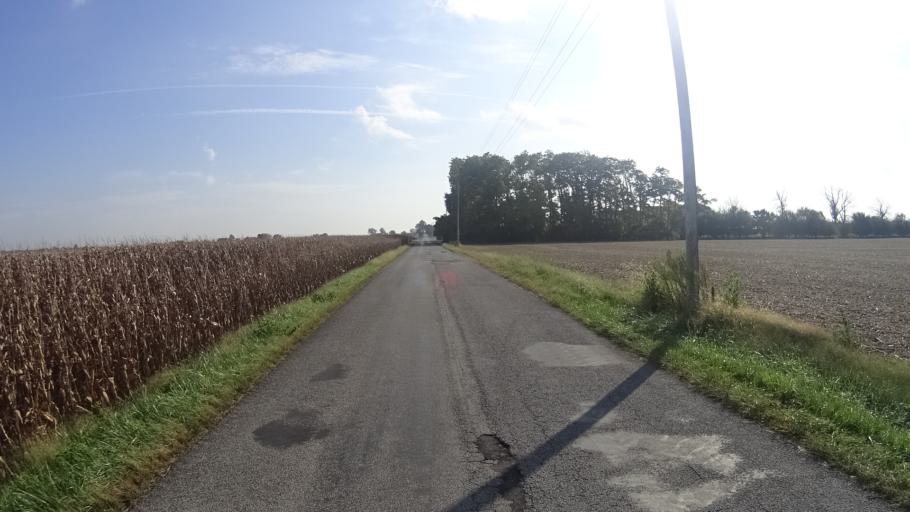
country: US
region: Indiana
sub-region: Madison County
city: Lapel
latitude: 40.0457
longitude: -85.8296
